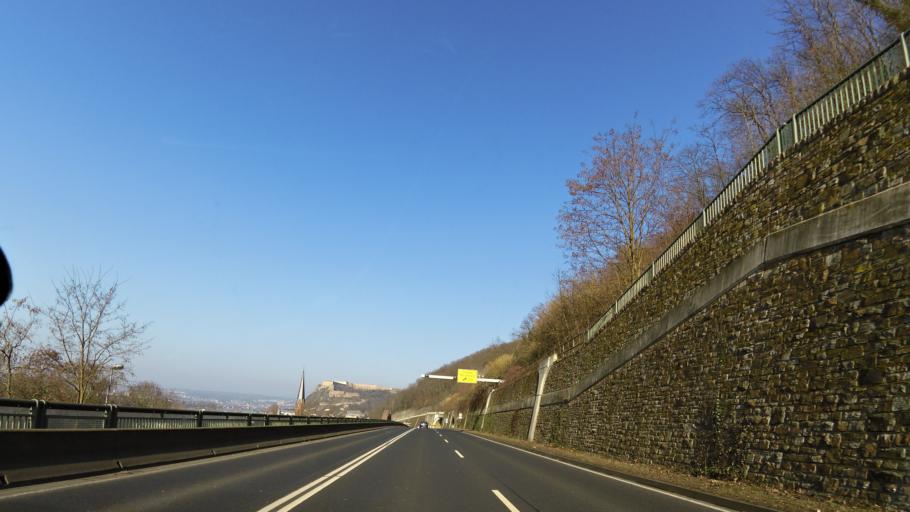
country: DE
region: Rheinland-Pfalz
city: Koblenz
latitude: 50.3510
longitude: 7.6087
